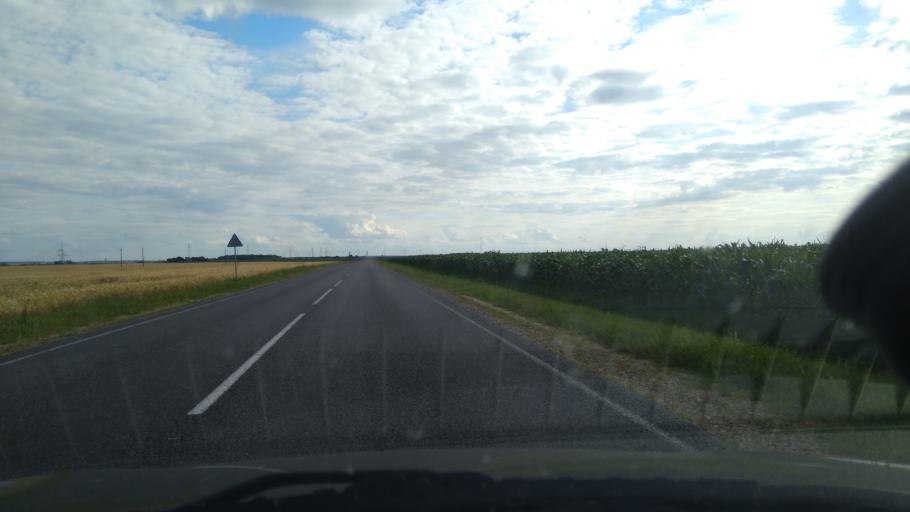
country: BY
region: Grodnenskaya
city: Masty
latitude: 53.3089
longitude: 24.6949
